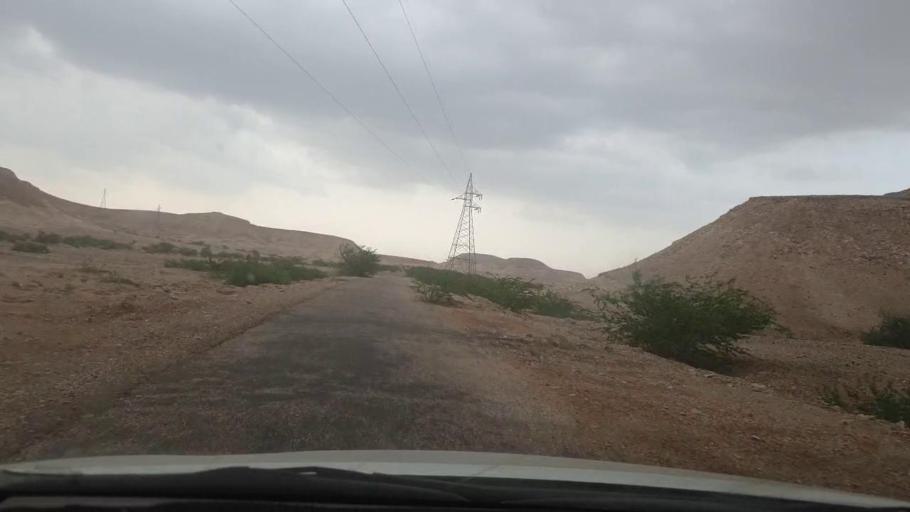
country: PK
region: Sindh
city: Khairpur
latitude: 27.4664
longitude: 68.9223
